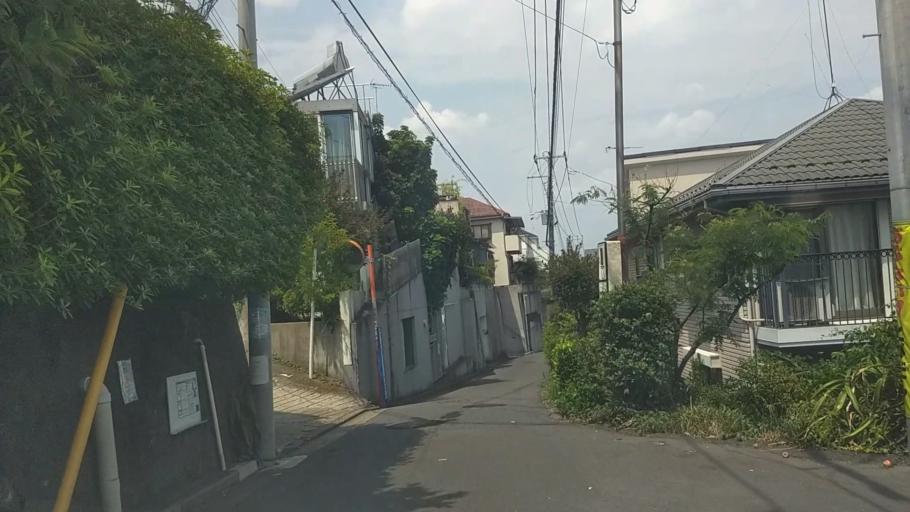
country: JP
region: Kanagawa
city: Yokohama
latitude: 35.5067
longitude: 139.6263
